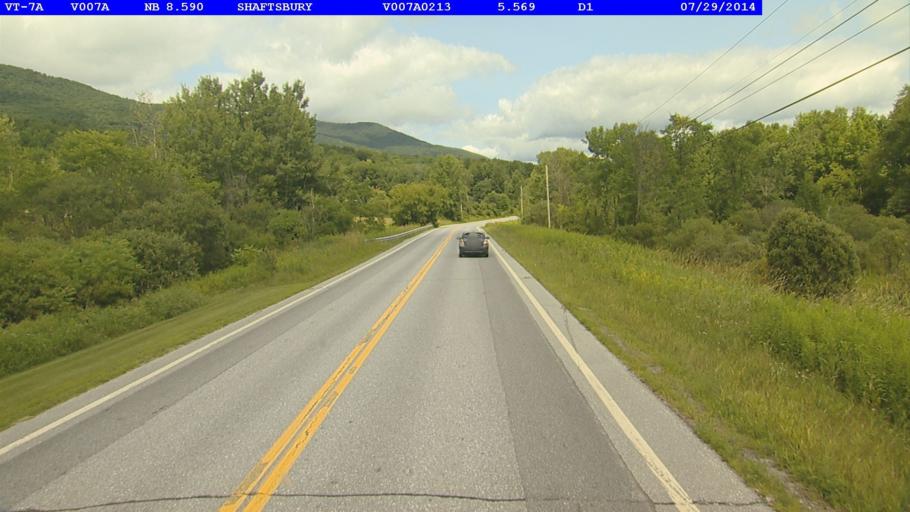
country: US
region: Vermont
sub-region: Bennington County
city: Arlington
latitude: 43.0103
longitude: -73.1954
